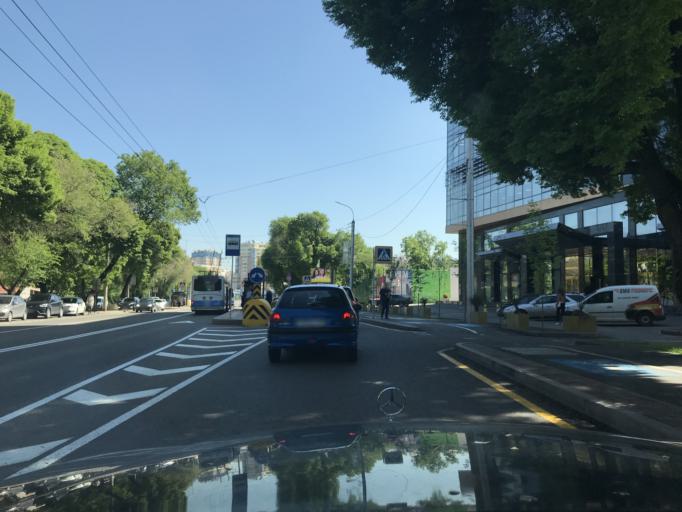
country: KZ
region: Almaty Qalasy
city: Almaty
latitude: 43.2301
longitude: 76.9330
